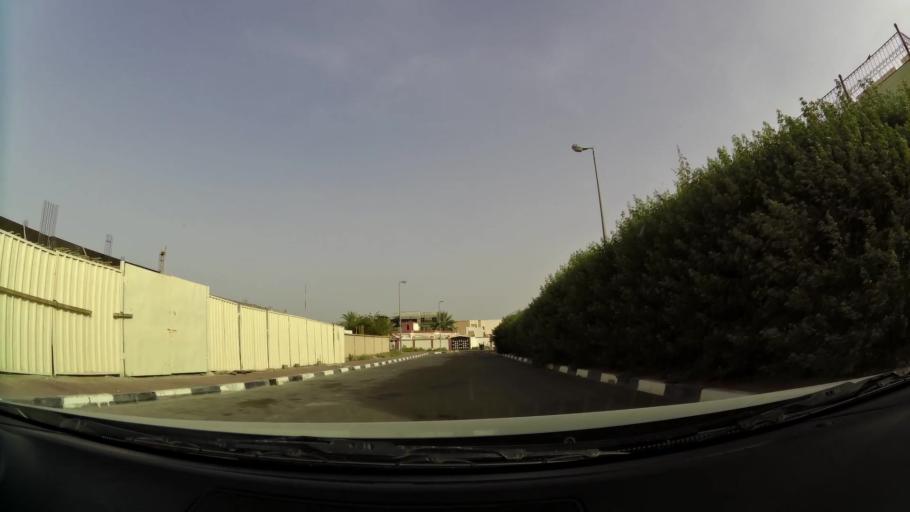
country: AE
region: Abu Dhabi
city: Al Ain
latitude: 24.2185
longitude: 55.6662
